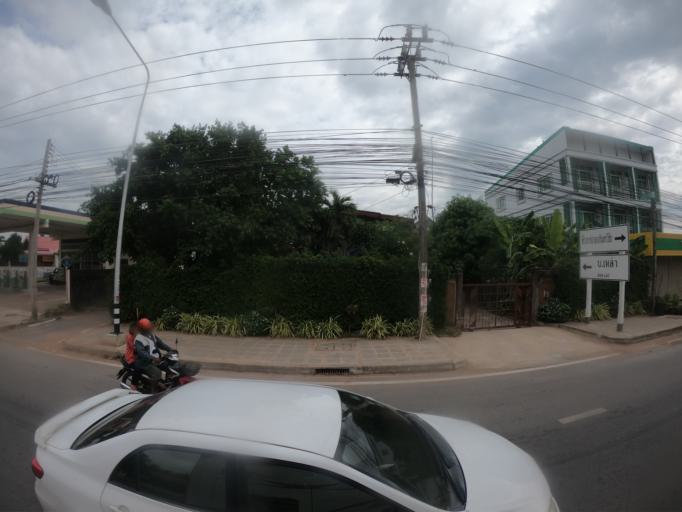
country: TH
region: Maha Sarakham
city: Kantharawichai
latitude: 16.3217
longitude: 103.2991
